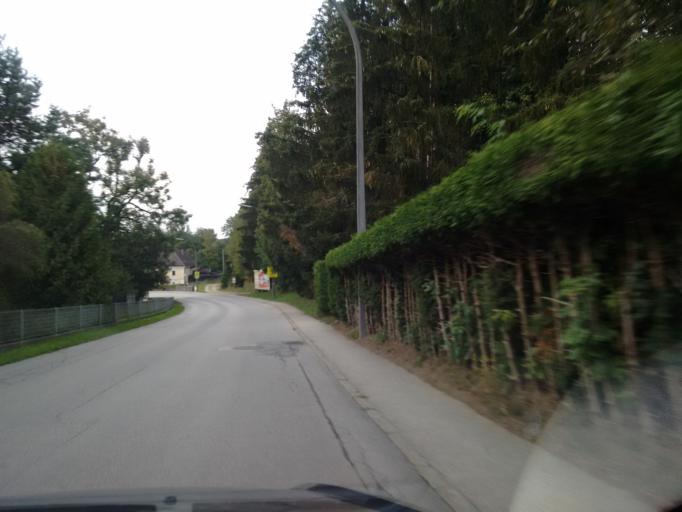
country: AT
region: Upper Austria
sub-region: Politischer Bezirk Steyr-Land
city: Bad Hall
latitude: 48.0369
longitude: 14.2031
